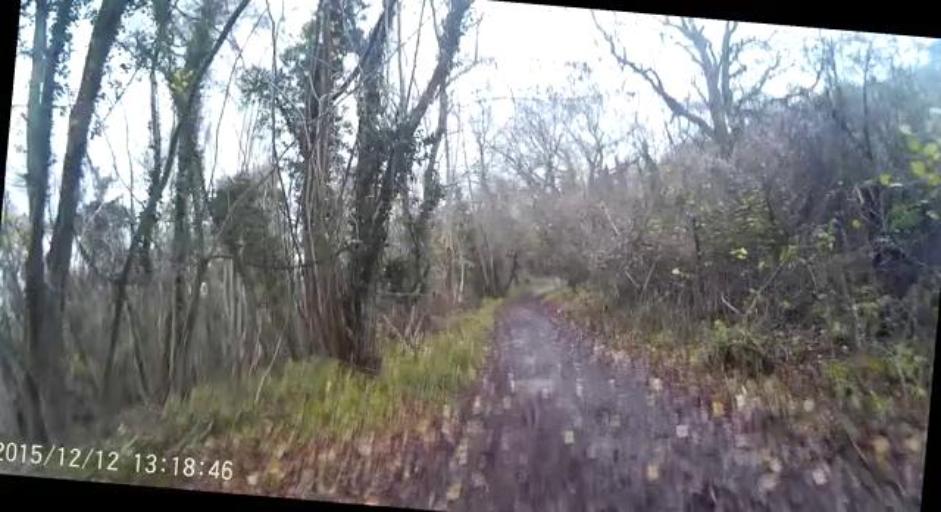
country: GB
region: England
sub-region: Hampshire
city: Petersfield
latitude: 50.9603
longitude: -0.8858
